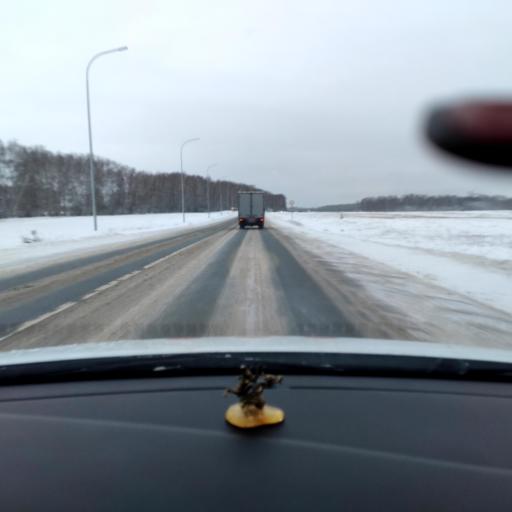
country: RU
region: Tatarstan
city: Vysokaya Gora
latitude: 55.9696
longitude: 49.4435
